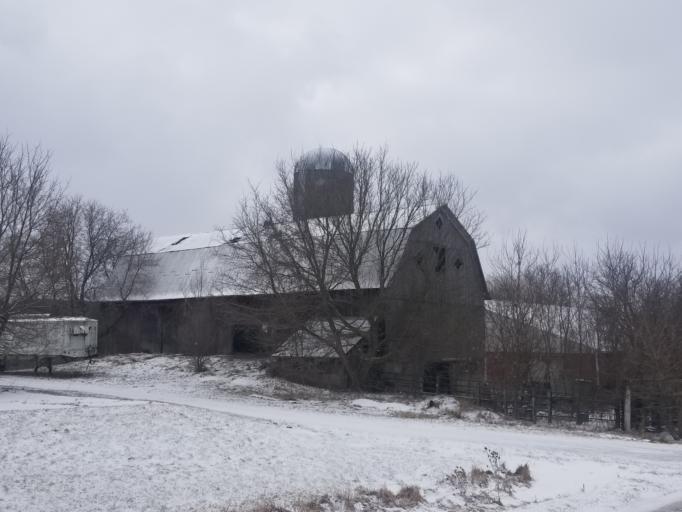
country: US
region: Michigan
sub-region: Osceola County
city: Evart
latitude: 43.8008
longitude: -85.3648
